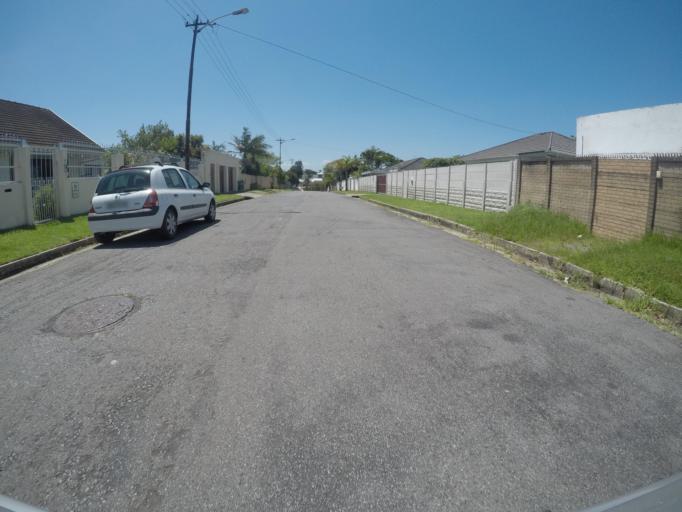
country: ZA
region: Eastern Cape
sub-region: Buffalo City Metropolitan Municipality
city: East London
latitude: -32.9874
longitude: 27.9065
